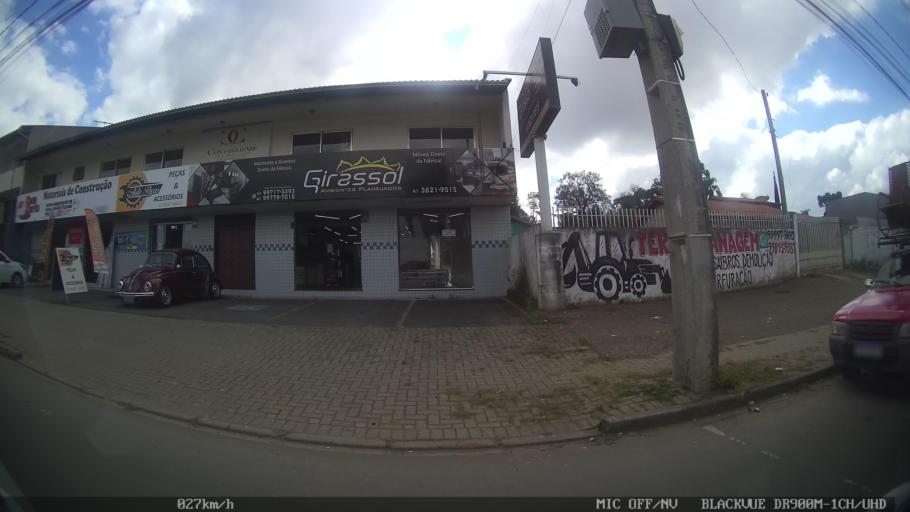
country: BR
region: Parana
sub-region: Colombo
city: Colombo
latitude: -25.3479
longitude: -49.2005
